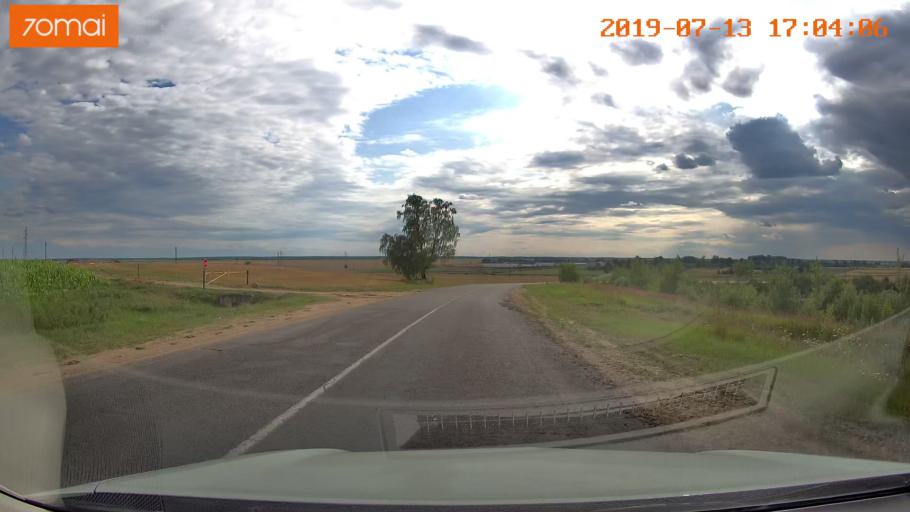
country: BY
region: Mogilev
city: Kirawsk
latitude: 53.2714
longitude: 29.3724
